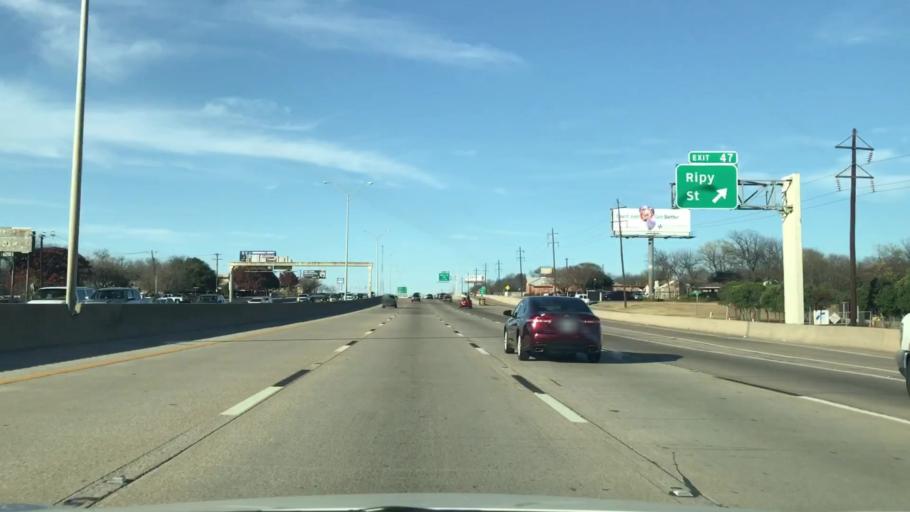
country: US
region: Texas
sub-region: Tarrant County
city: Fort Worth
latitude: 32.6918
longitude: -97.3205
